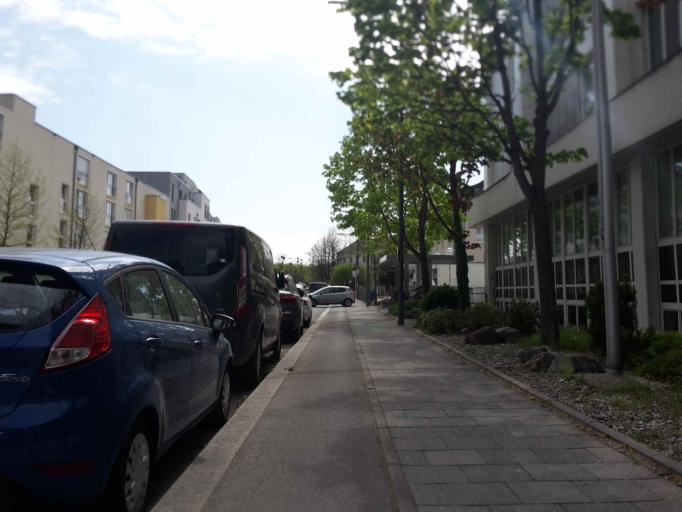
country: DE
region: Bavaria
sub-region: Upper Bavaria
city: Karlsfeld
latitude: 48.1766
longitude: 11.5052
